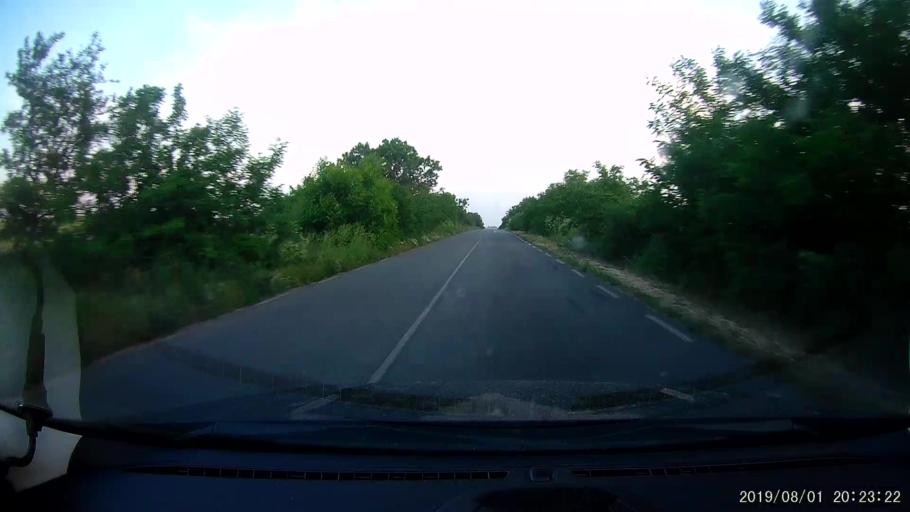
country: BG
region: Yambol
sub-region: Obshtina Elkhovo
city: Elkhovo
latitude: 42.2501
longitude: 26.5988
